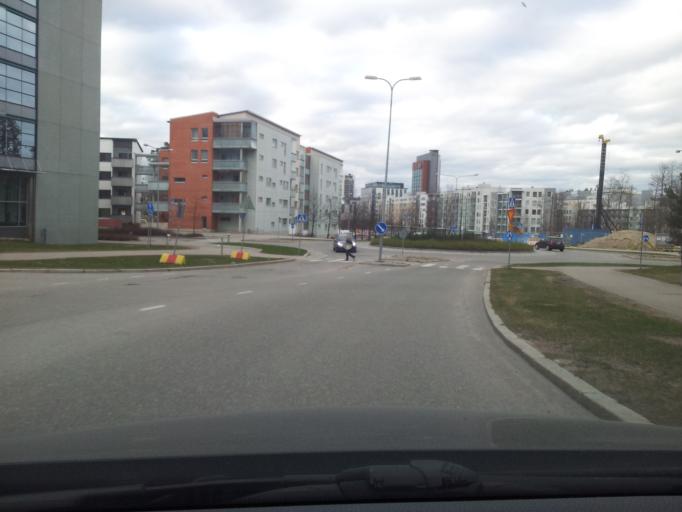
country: FI
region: Uusimaa
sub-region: Helsinki
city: Kilo
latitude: 60.2133
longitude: 24.8103
